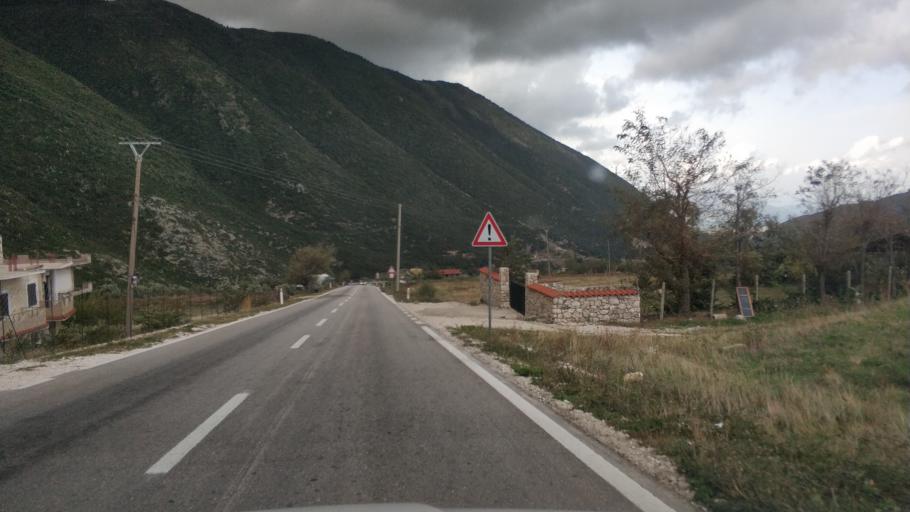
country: AL
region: Vlore
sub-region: Rrethi i Vlores
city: Brataj
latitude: 40.2317
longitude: 19.5657
